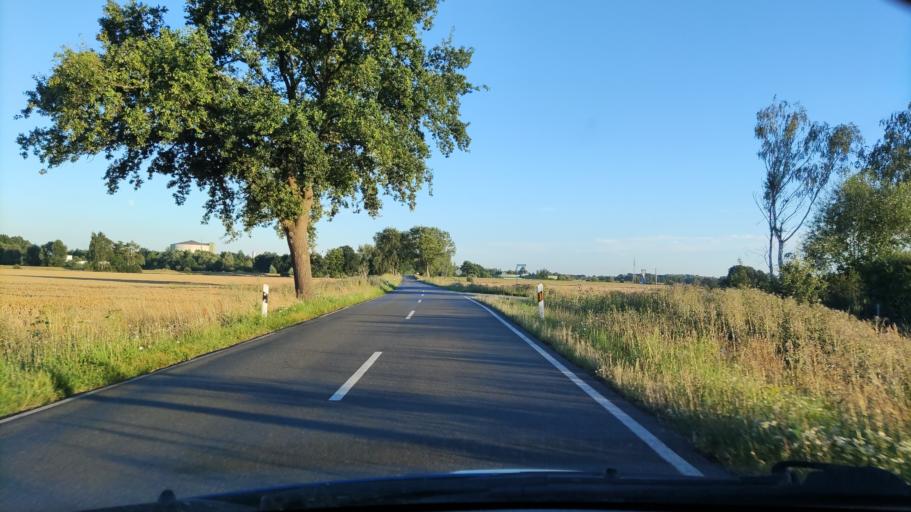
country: DE
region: Lower Saxony
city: Luechow
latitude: 52.9912
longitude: 11.1549
